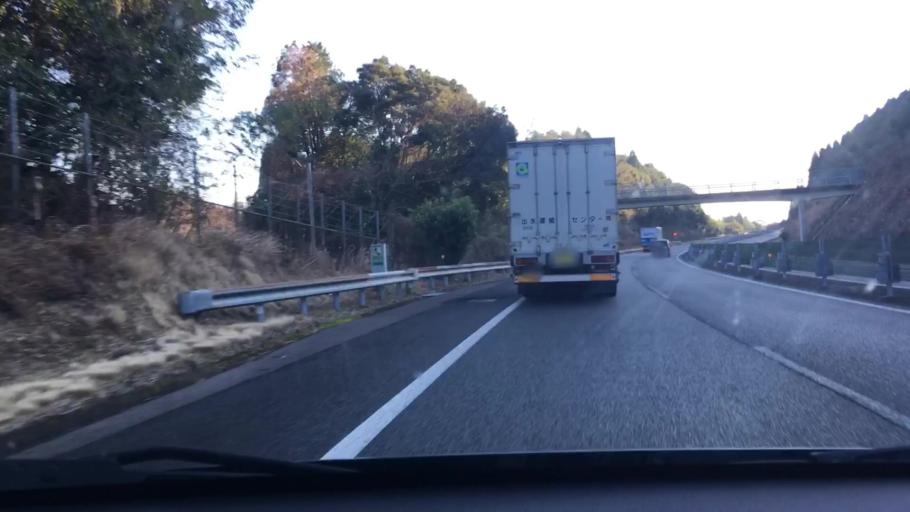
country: JP
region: Kagoshima
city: Kajiki
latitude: 31.8295
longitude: 130.6938
